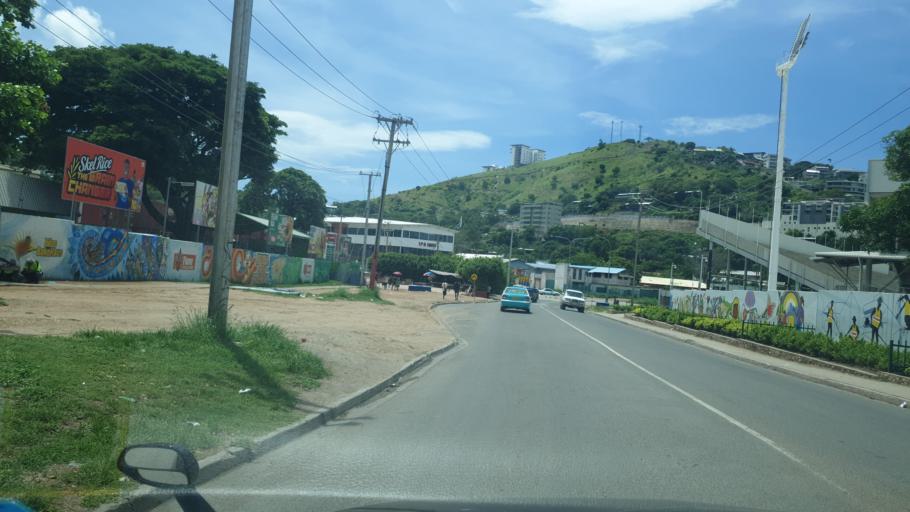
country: PG
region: National Capital
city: Port Moresby
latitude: -9.4659
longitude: 147.1581
